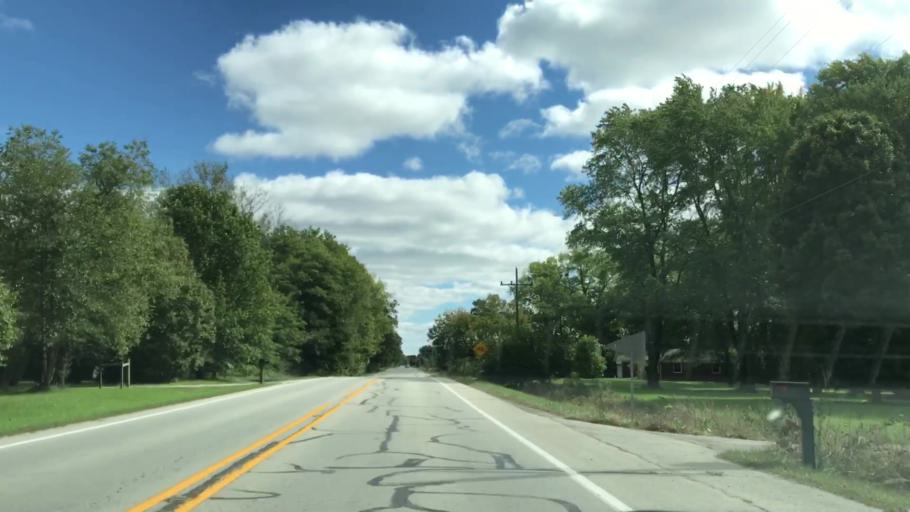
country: US
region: Indiana
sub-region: Hamilton County
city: Westfield
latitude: 40.0878
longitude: -86.1130
